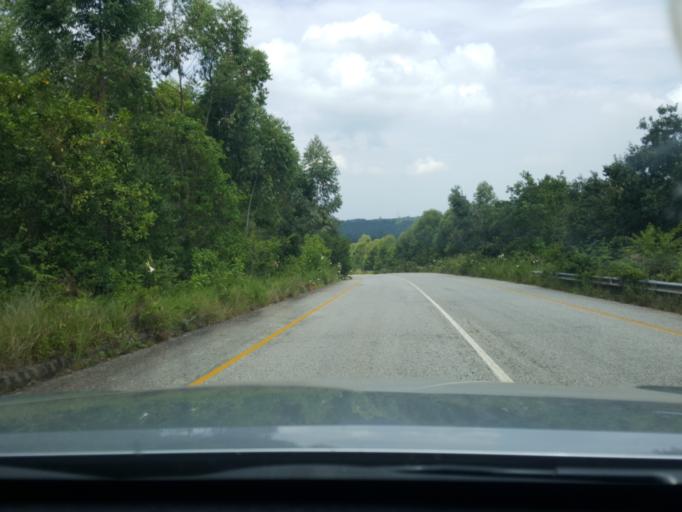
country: ZA
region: Mpumalanga
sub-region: Ehlanzeni District
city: White River
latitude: -25.1943
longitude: 30.9128
